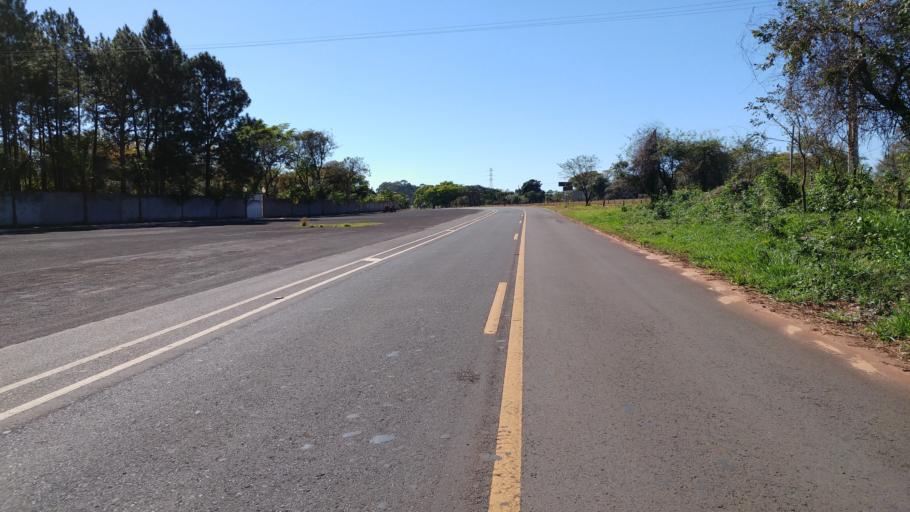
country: BR
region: Sao Paulo
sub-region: Paraguacu Paulista
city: Paraguacu Paulista
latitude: -22.4198
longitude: -50.6047
